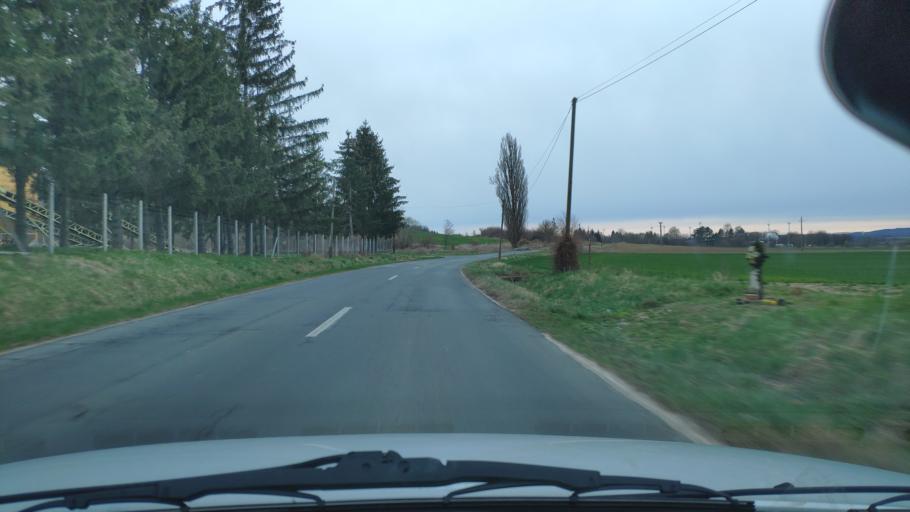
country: HU
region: Zala
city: Nagykanizsa
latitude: 46.5525
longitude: 16.9892
